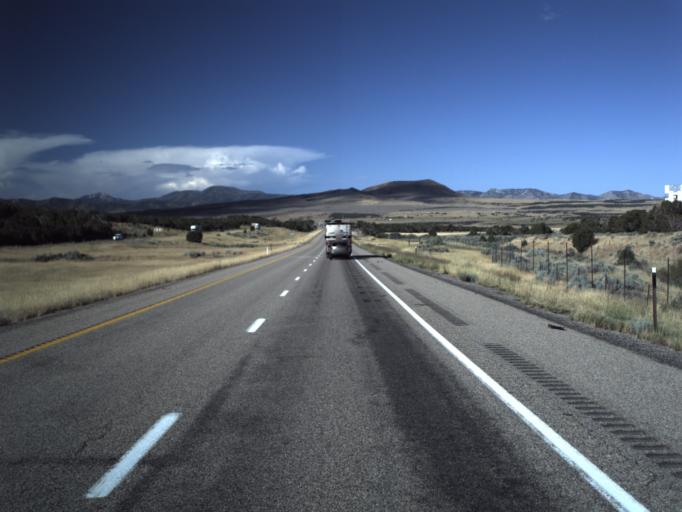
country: US
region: Utah
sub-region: Beaver County
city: Beaver
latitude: 38.6001
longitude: -112.5593
